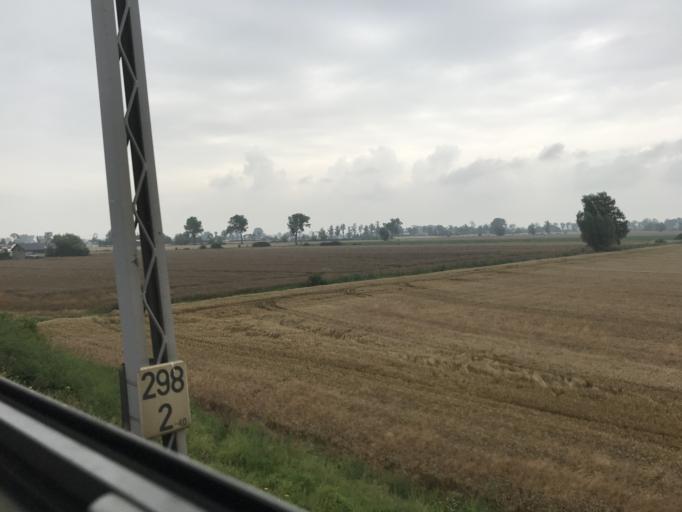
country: PL
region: Pomeranian Voivodeship
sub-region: Powiat tczewski
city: Tczew
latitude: 54.1126
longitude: 18.7759
